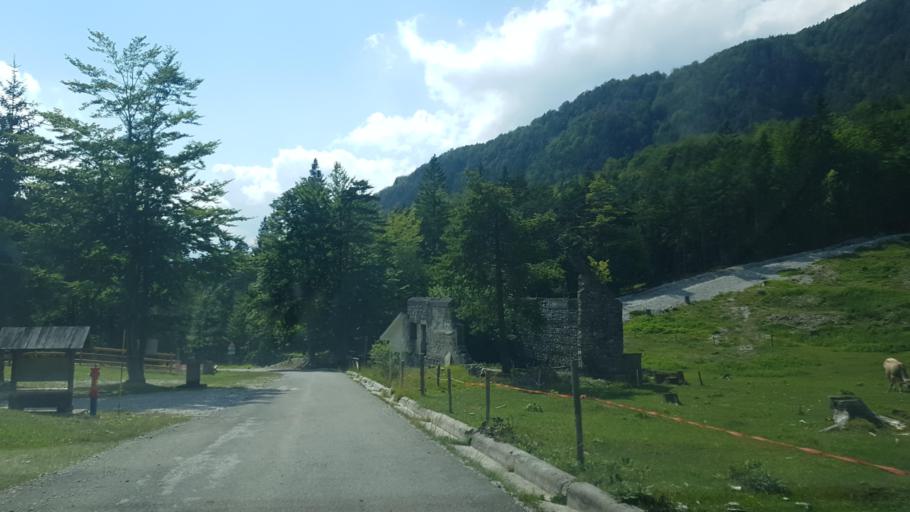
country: IT
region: Friuli Venezia Giulia
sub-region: Provincia di Udine
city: Malborghetto
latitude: 46.4610
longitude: 13.4226
